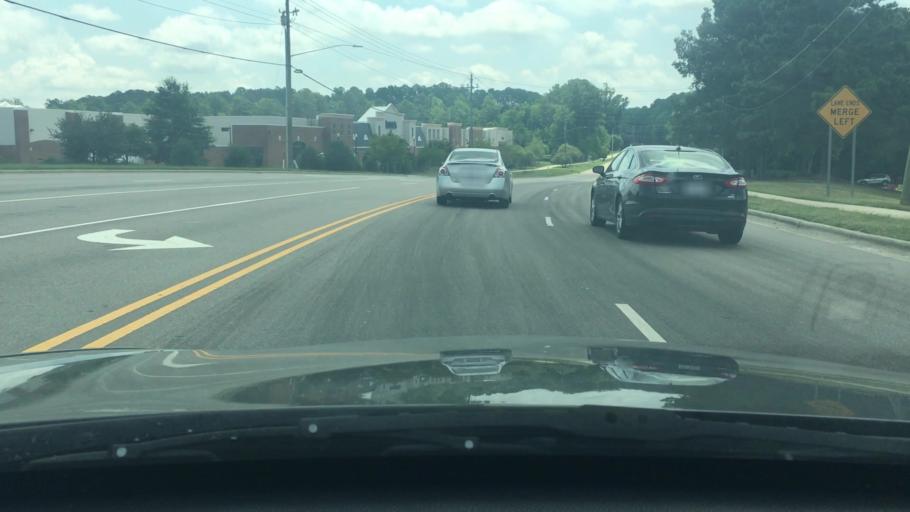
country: US
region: North Carolina
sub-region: Wake County
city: Cary
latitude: 35.7985
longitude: -78.7957
